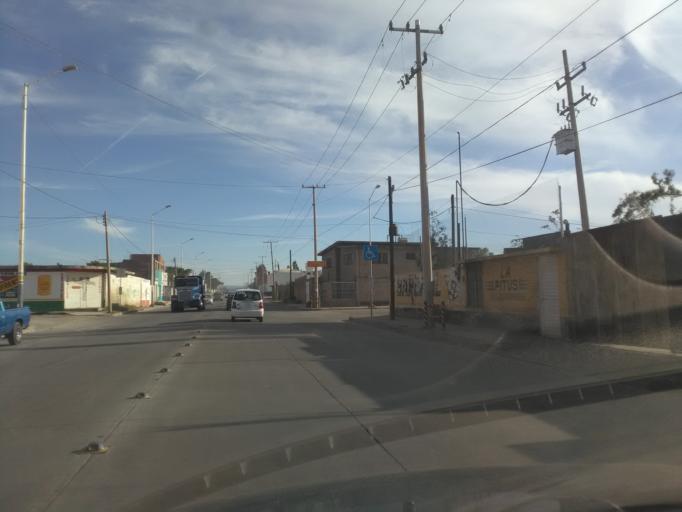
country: MX
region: Durango
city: Victoria de Durango
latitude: 24.0170
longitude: -104.6220
